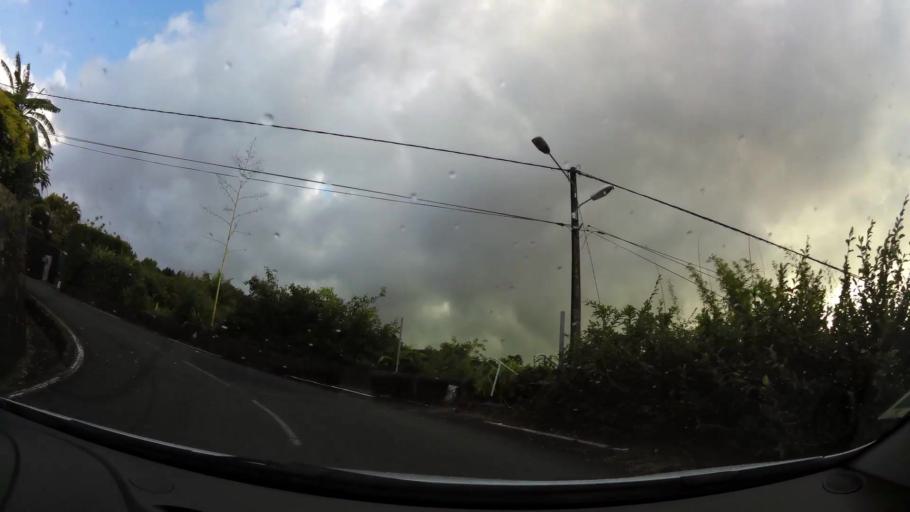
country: RE
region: Reunion
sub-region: Reunion
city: Saint-Denis
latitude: -20.9135
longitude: 55.4396
